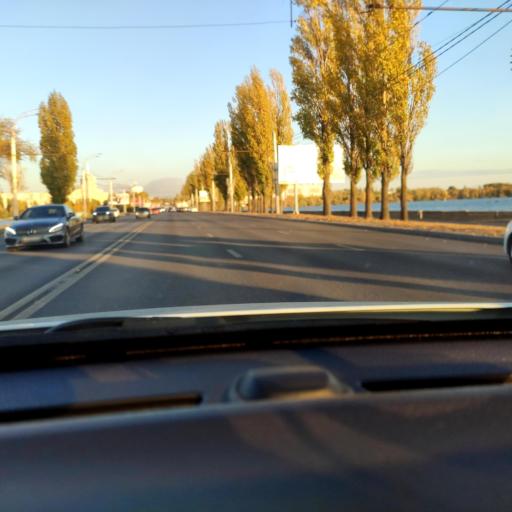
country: RU
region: Voronezj
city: Voronezh
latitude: 51.6663
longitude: 39.2298
